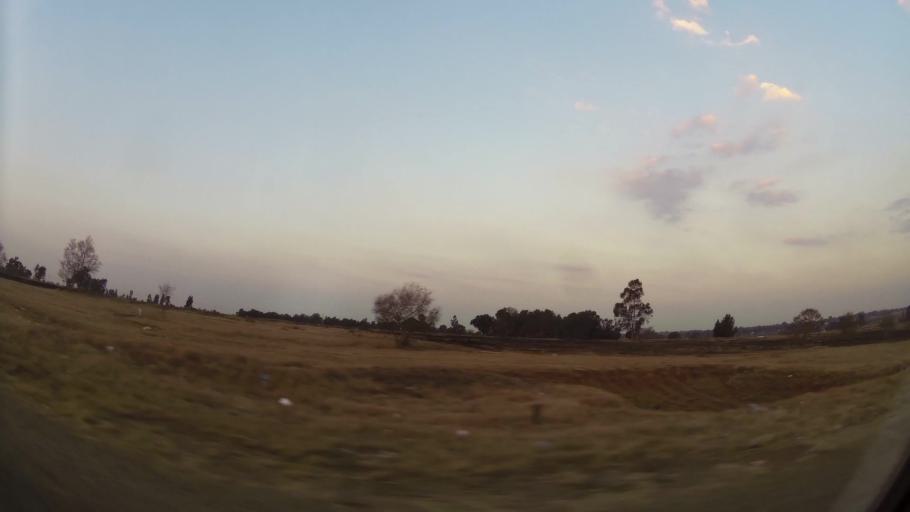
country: ZA
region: Gauteng
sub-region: Ekurhuleni Metropolitan Municipality
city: Springs
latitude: -26.2817
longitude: 28.4296
